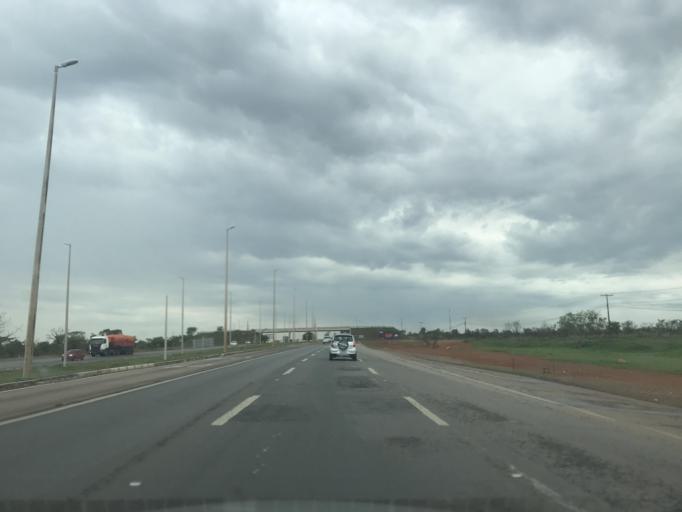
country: BR
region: Federal District
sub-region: Brasilia
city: Brasilia
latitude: -15.9698
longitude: -47.9913
